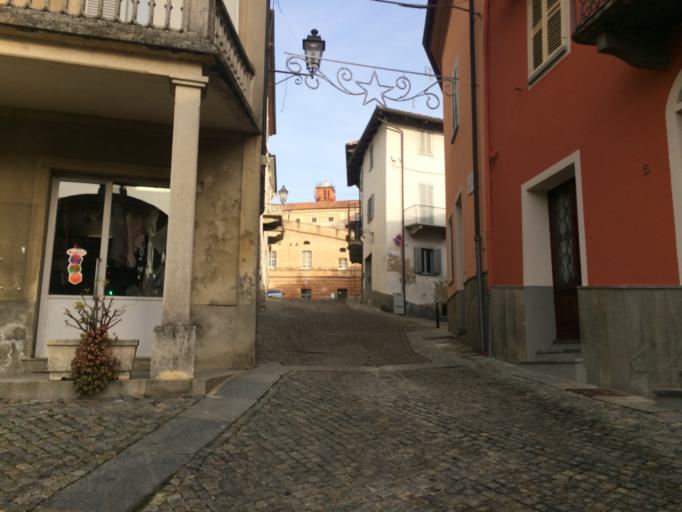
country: IT
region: Piedmont
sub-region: Provincia di Cuneo
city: Govone
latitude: 44.8037
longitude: 8.0999
